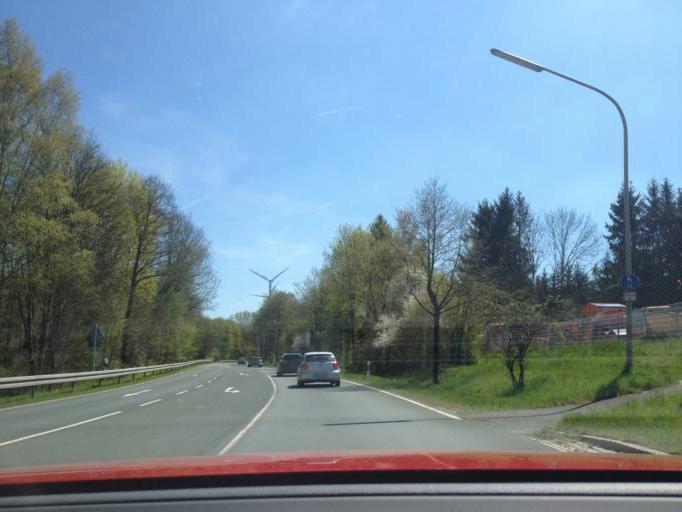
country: DE
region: Bavaria
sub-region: Upper Franconia
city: Oberkotzau
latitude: 50.2555
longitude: 11.9349
